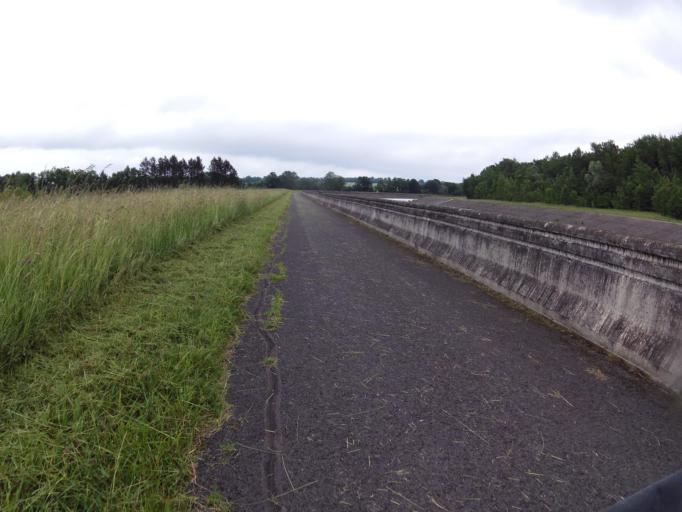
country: FR
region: Champagne-Ardenne
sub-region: Departement de la Haute-Marne
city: Villiers-en-Lieu
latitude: 48.6117
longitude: 4.8671
